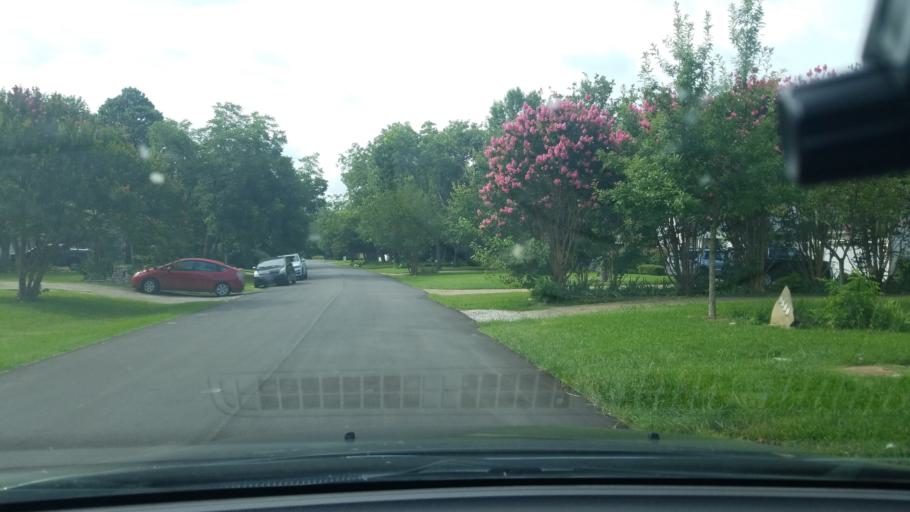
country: US
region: Texas
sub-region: Dallas County
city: Highland Park
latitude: 32.8268
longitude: -96.7019
